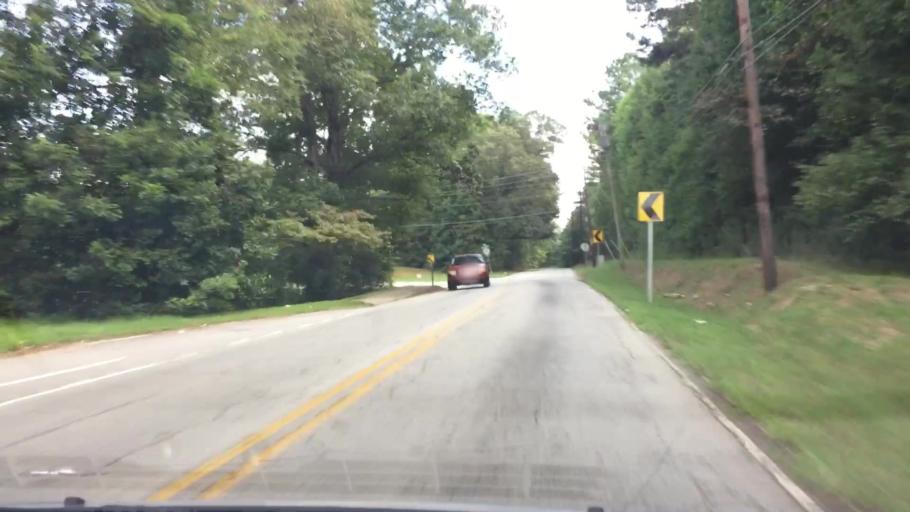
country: US
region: Georgia
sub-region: DeKalb County
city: Gresham Park
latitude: 33.6918
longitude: -84.3215
